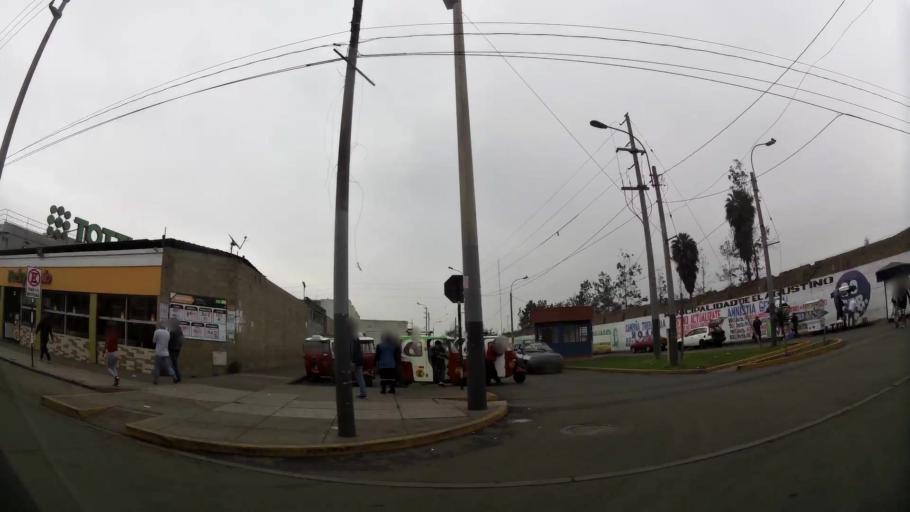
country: PE
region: Lima
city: Lima
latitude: -12.0405
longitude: -76.9994
